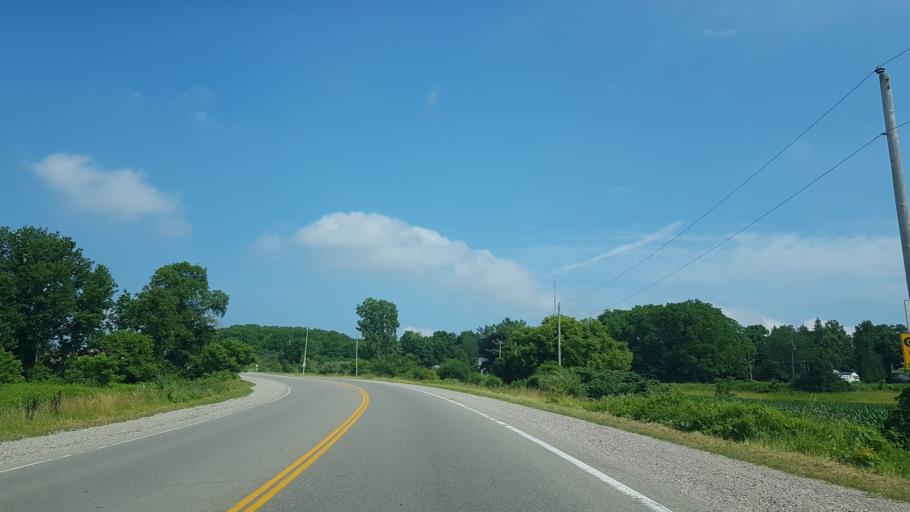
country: CA
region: Ontario
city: Delaware
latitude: 42.9636
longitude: -81.3731
